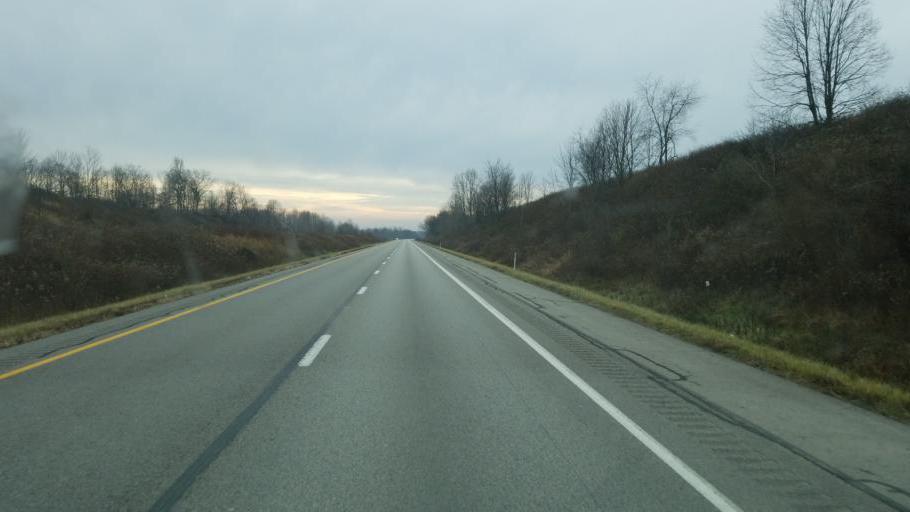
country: US
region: Pennsylvania
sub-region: Mercer County
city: Stoneboro
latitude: 41.3102
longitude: -80.1588
